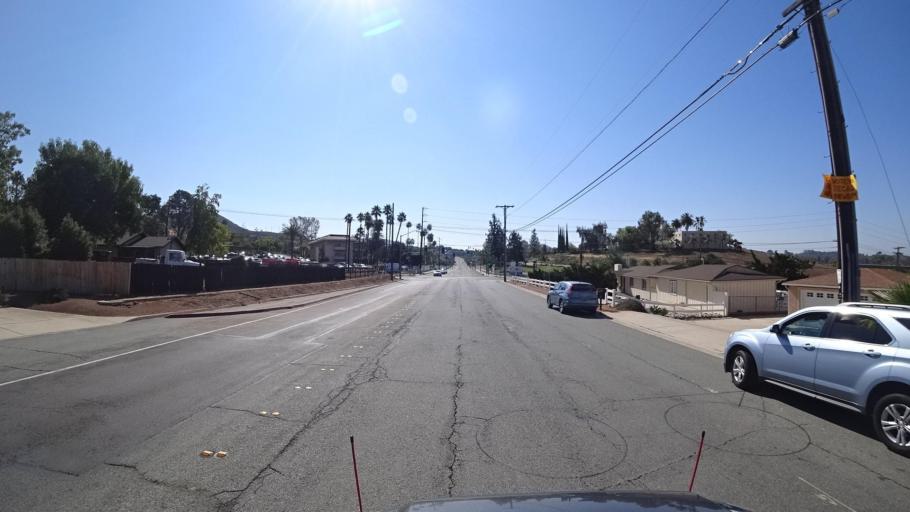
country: US
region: California
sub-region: San Diego County
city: Granite Hills
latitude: 32.8017
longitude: -116.9052
